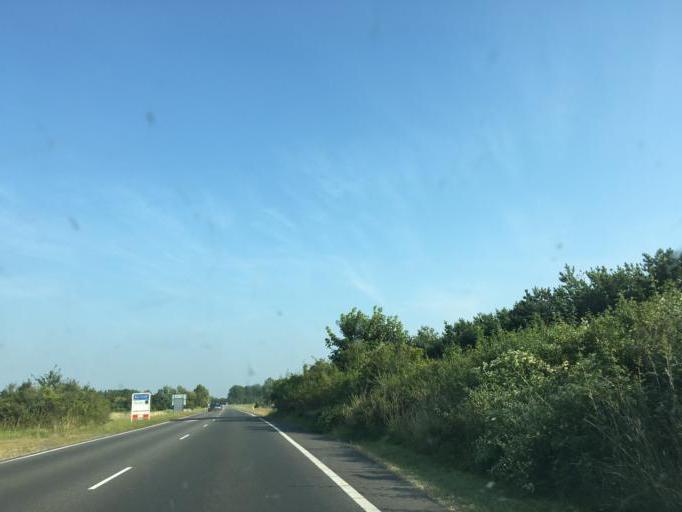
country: NL
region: South Holland
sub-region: Gemeente Noordwijk
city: Noordwijk-Binnen
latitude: 52.2271
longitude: 4.4457
